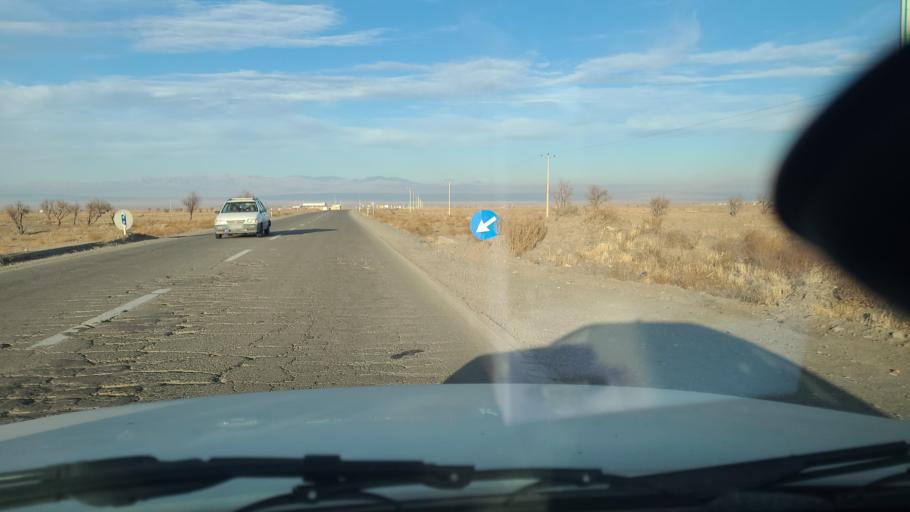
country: IR
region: Razavi Khorasan
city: Neqab
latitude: 36.5020
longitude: 57.5322
